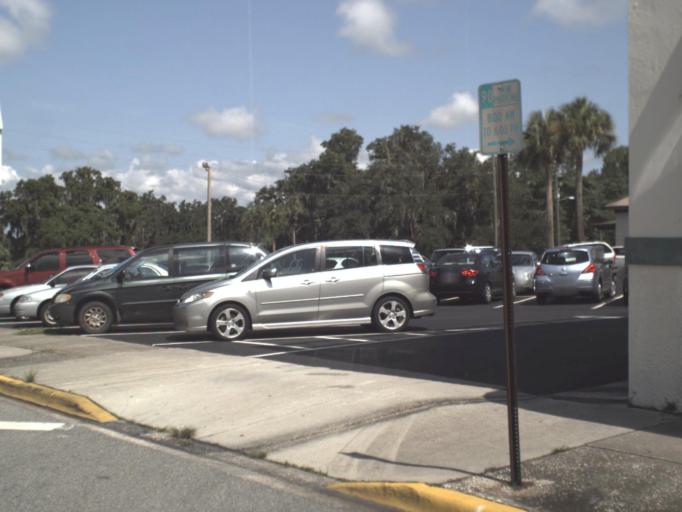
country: US
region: Florida
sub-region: Hernando County
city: Brooksville
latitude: 28.5556
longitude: -82.3882
